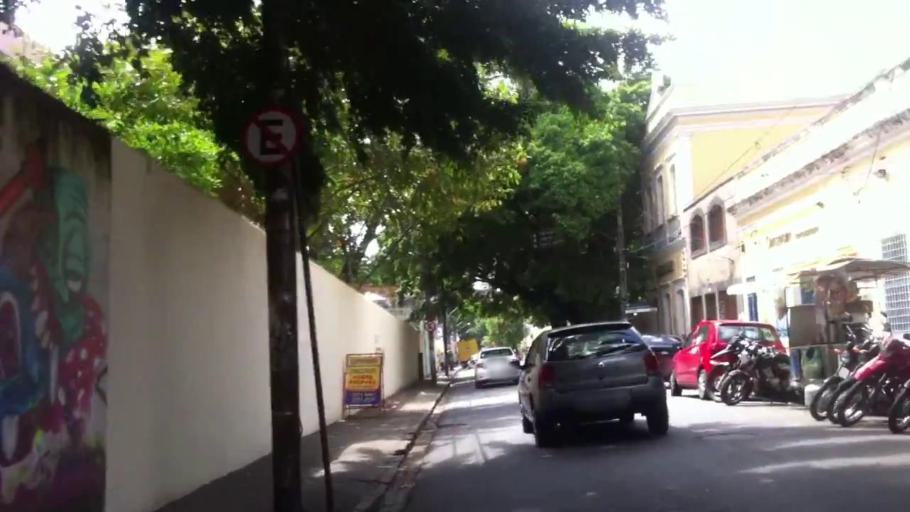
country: BR
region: Pernambuco
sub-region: Recife
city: Recife
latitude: -8.0576
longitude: -34.8868
